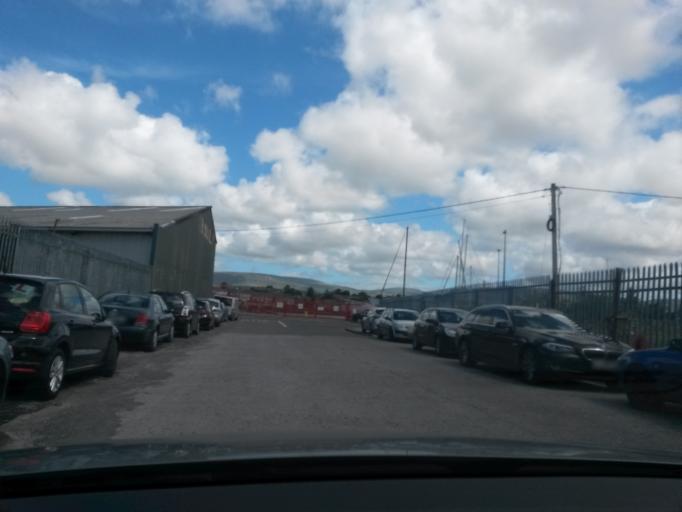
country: IE
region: Connaught
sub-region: Sligo
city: Sligo
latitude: 54.2751
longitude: -8.4803
